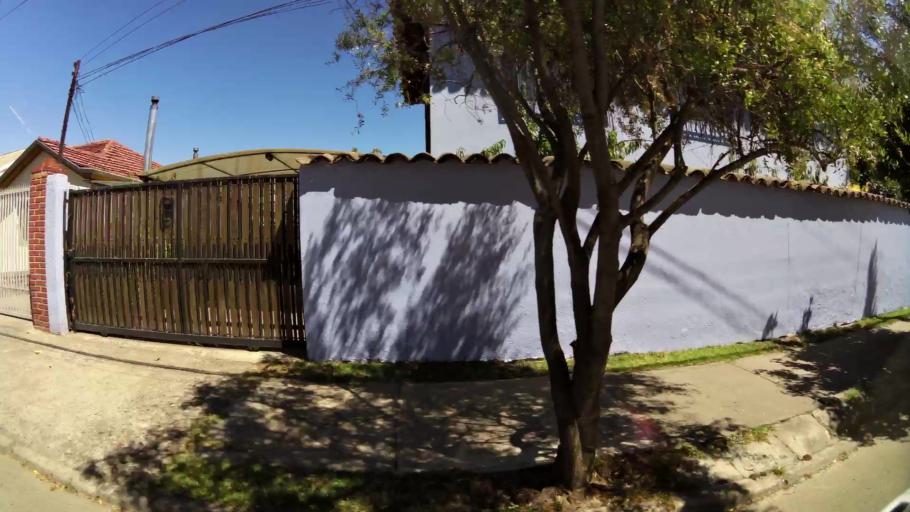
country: CL
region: O'Higgins
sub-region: Provincia de Cachapoal
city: Rancagua
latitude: -34.1621
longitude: -70.7476
